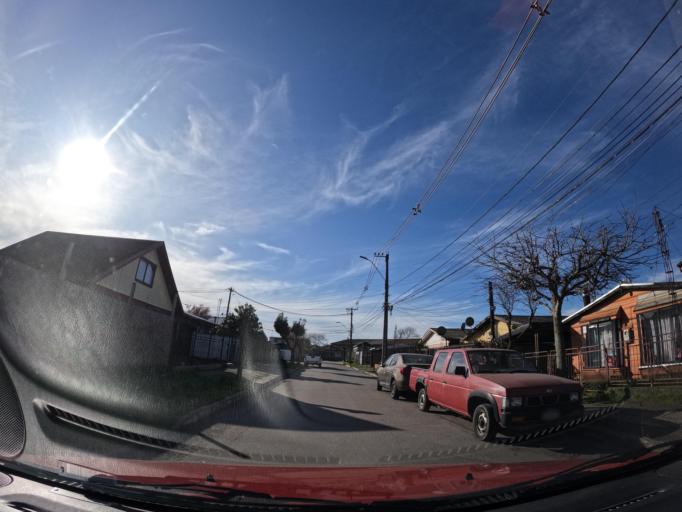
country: CL
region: Biobio
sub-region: Provincia de Concepcion
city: Talcahuano
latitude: -36.7702
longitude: -73.0821
